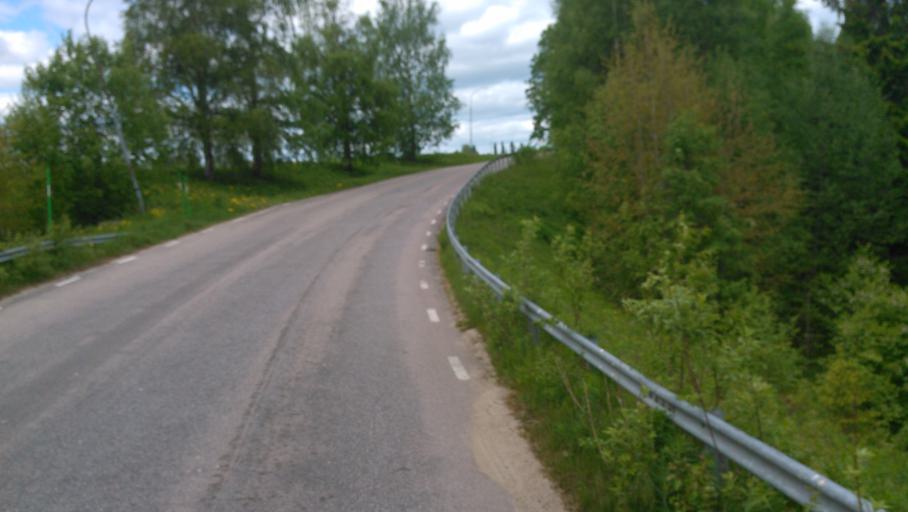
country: SE
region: Vaesterbotten
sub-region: Umea Kommun
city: Roback
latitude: 63.8697
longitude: 20.0671
